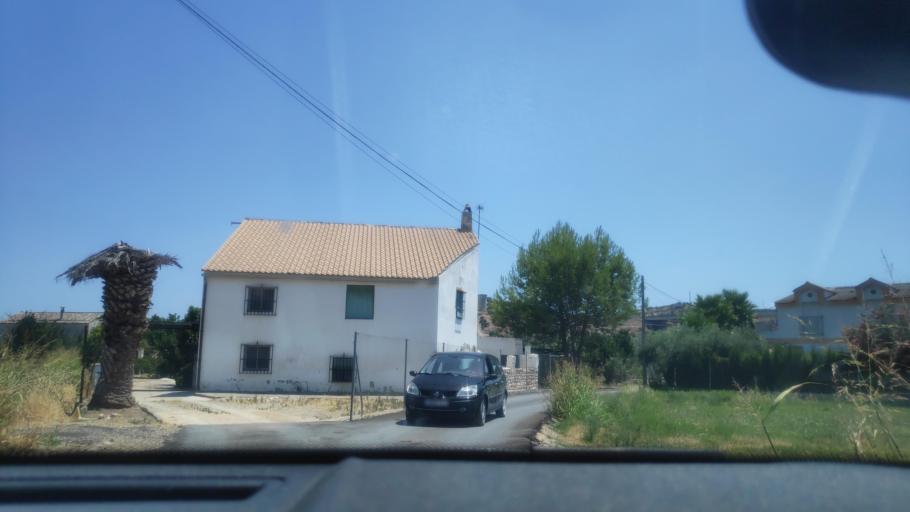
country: ES
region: Andalusia
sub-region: Provincia de Jaen
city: Jaen
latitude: 37.8237
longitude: -3.7585
